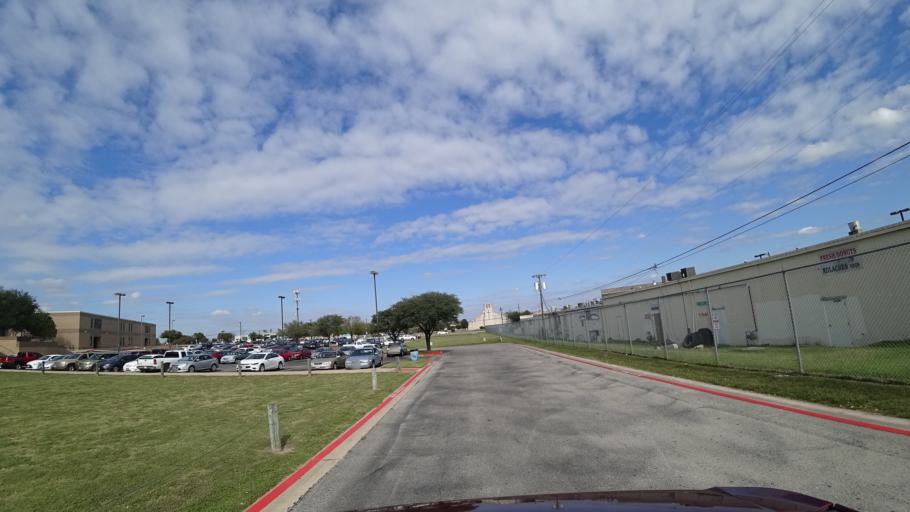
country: US
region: Texas
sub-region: Travis County
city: Pflugerville
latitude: 30.4430
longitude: -97.6312
